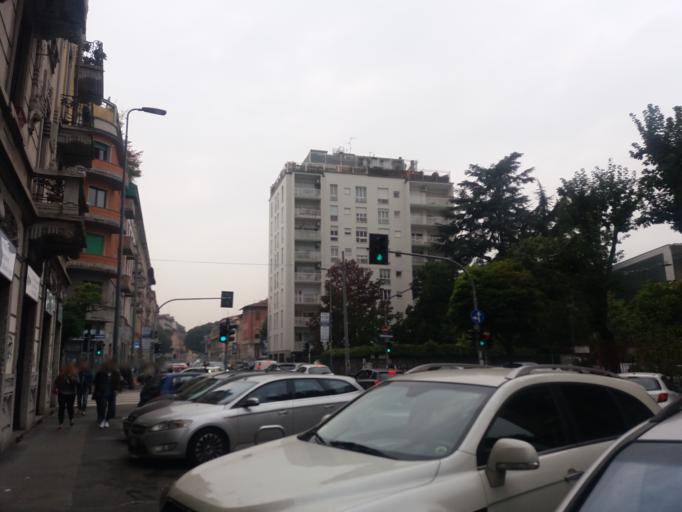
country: IT
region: Lombardy
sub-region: Citta metropolitana di Milano
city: Milano
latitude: 45.4844
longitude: 9.2269
